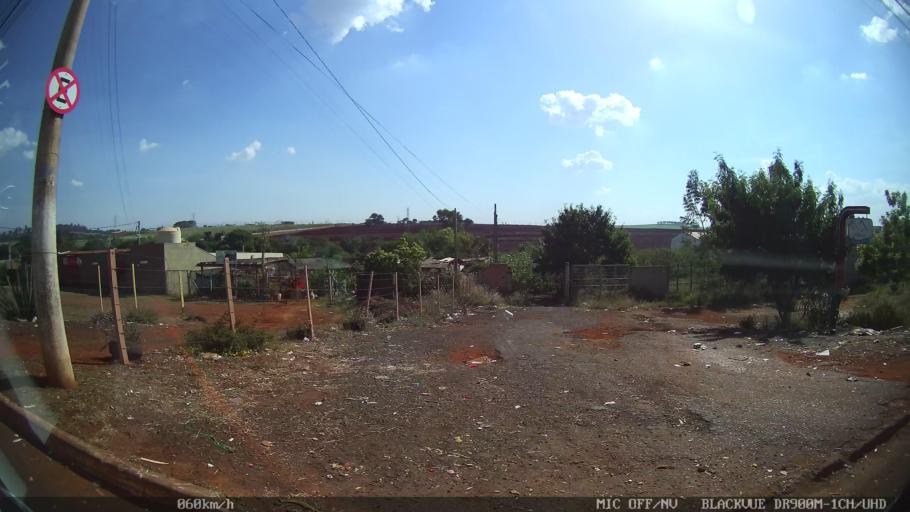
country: BR
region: Sao Paulo
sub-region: Ribeirao Preto
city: Ribeirao Preto
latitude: -21.2034
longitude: -47.8586
